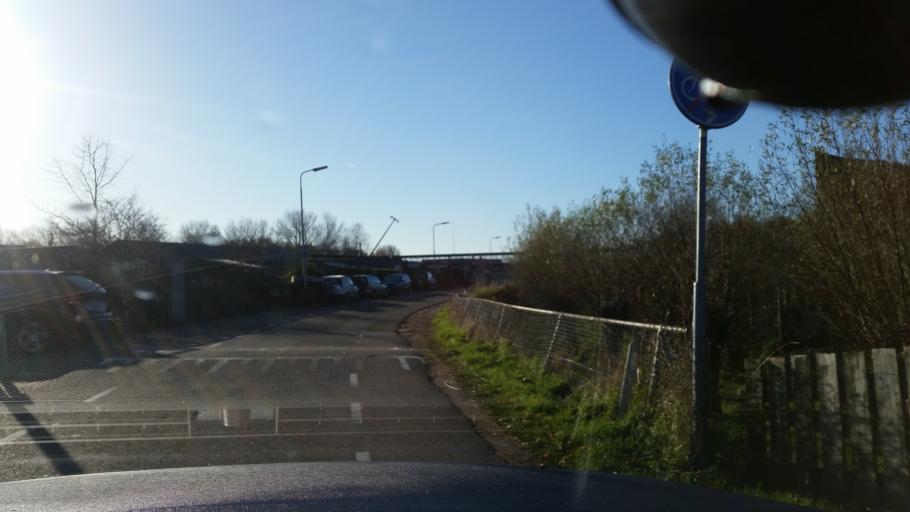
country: NL
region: North Holland
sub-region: Gemeente Ouder-Amstel
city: Ouderkerk aan de Amstel
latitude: 52.2908
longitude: 4.9176
